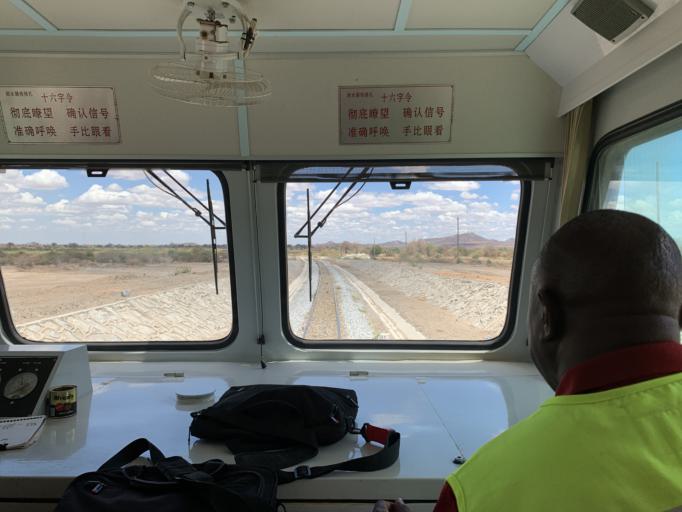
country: TZ
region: Dodoma
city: Dodoma
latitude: -6.1189
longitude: 35.5096
